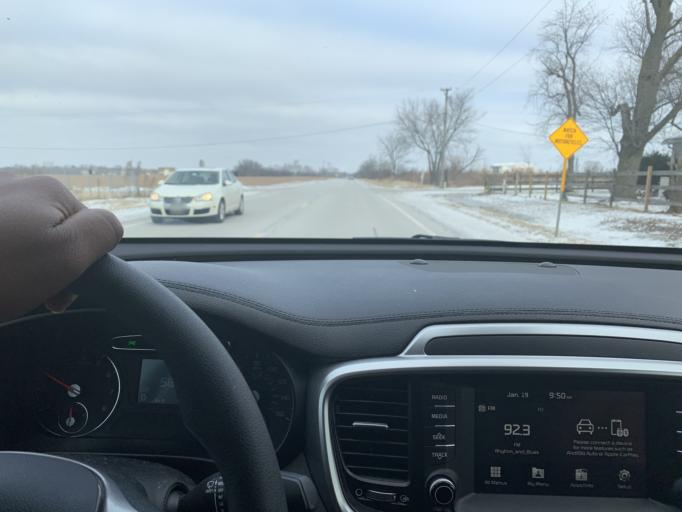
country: US
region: Illinois
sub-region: Will County
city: Fairmont
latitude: 41.5606
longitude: -88.0443
